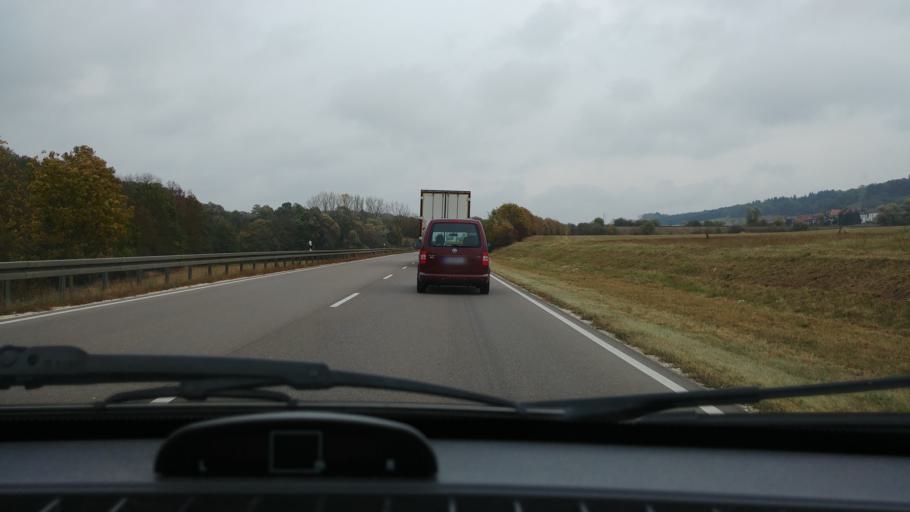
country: DE
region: Baden-Wuerttemberg
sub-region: Regierungsbezirk Stuttgart
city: Huttlingen
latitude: 48.8853
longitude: 10.1231
